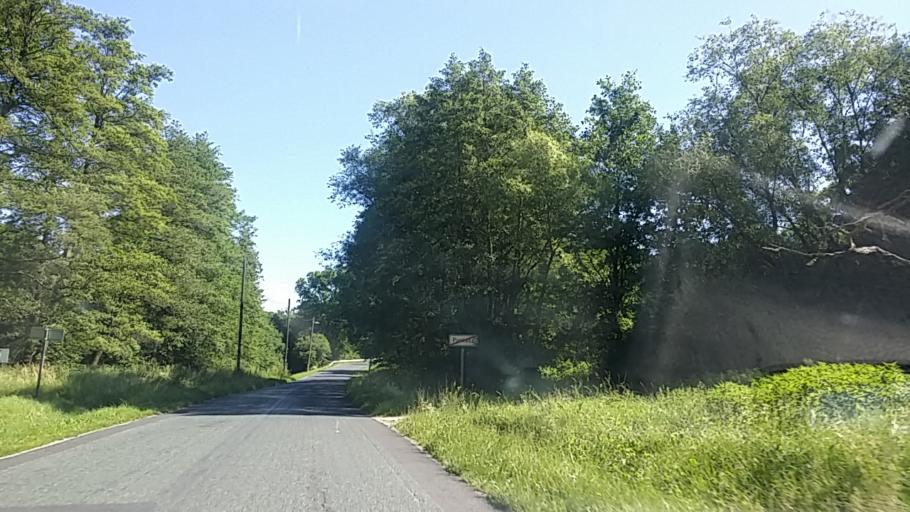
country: HU
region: Zala
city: Zalalovo
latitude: 46.8424
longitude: 16.5016
